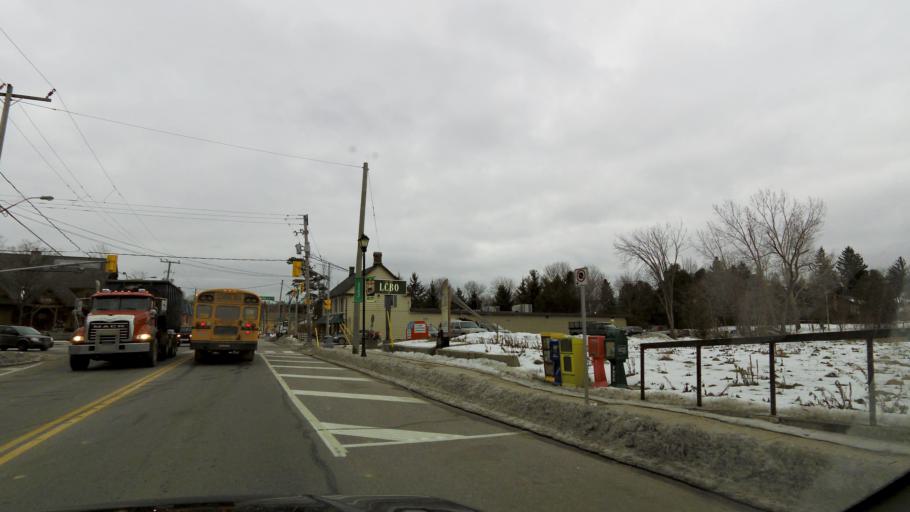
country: CA
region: Ontario
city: Brampton
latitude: 43.8705
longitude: -79.8676
